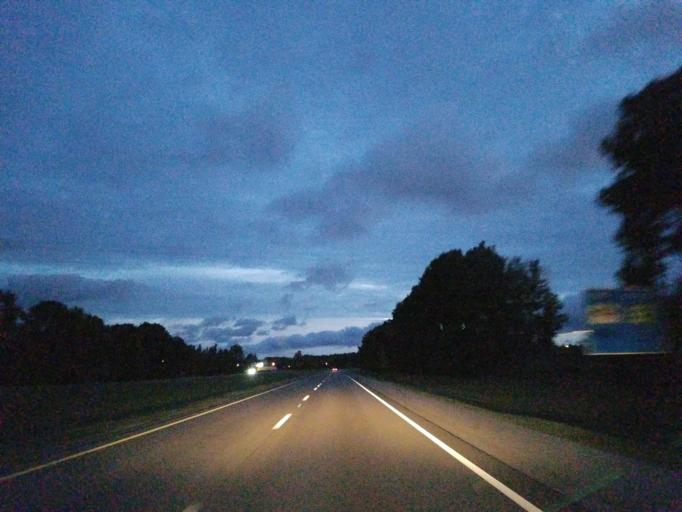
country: US
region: Mississippi
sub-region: Jones County
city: Sharon
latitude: 31.9166
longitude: -89.0065
